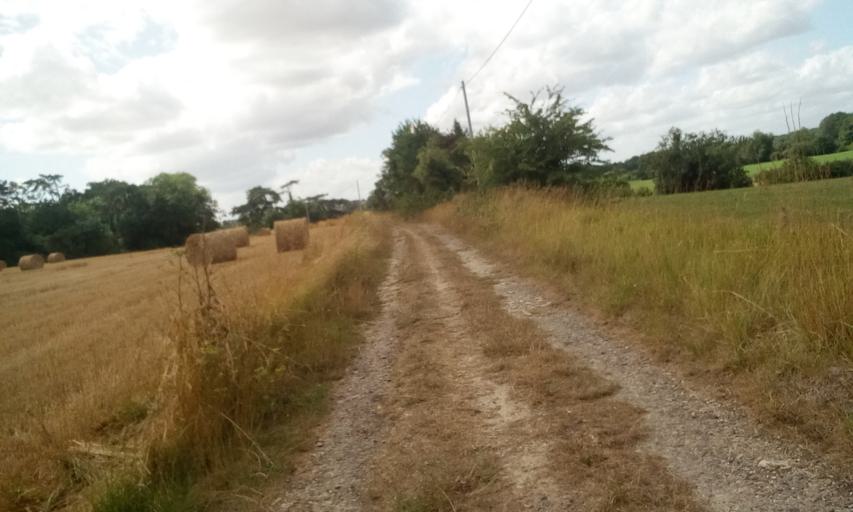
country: FR
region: Lower Normandy
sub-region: Departement du Calvados
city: Creully
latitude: 49.2892
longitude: -0.5180
